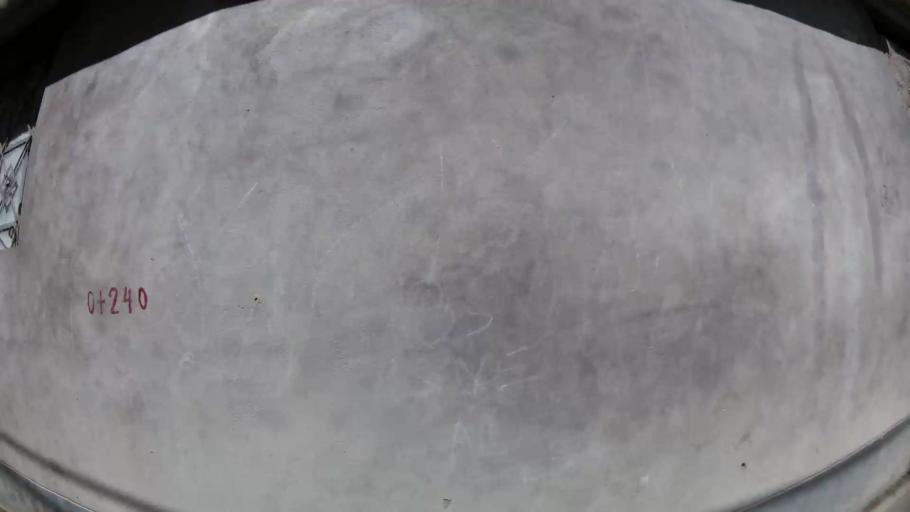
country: PE
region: Ayacucho
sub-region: Provincia de Huamanga
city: Carmen Alto
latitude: -13.1787
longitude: -74.2270
